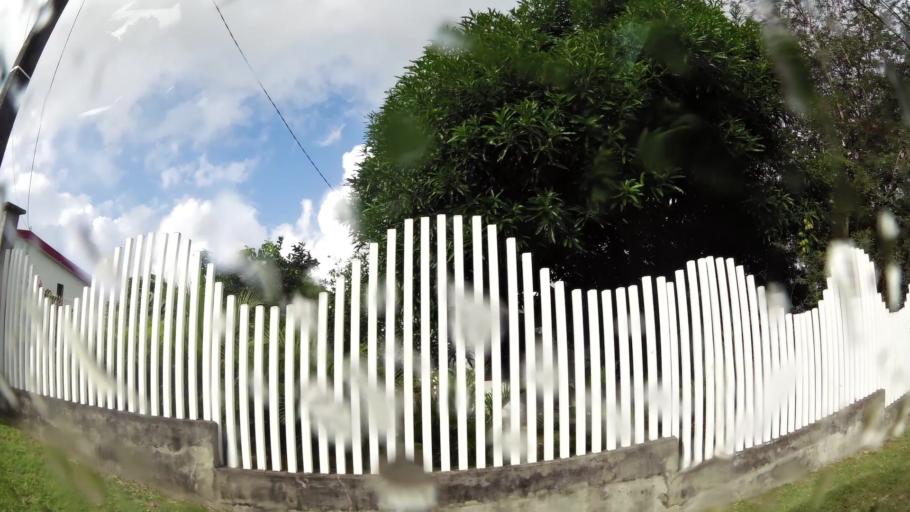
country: MQ
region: Martinique
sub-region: Martinique
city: Ducos
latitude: 14.5797
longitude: -60.9798
